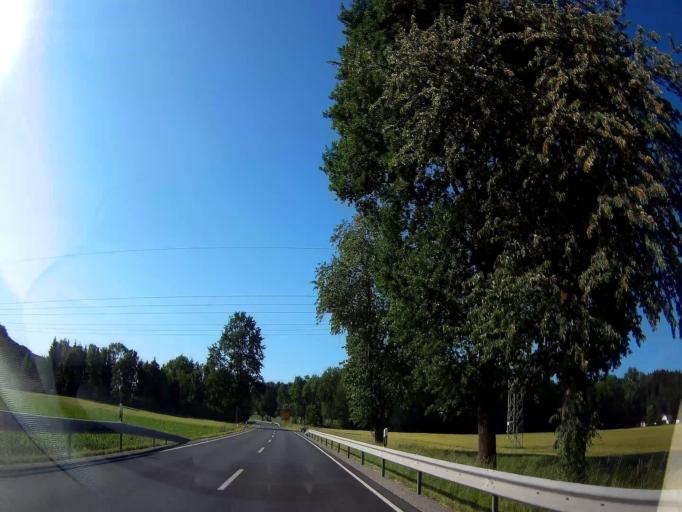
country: DE
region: Bavaria
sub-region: Upper Bavaria
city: Stammham
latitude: 48.2519
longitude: 12.9077
